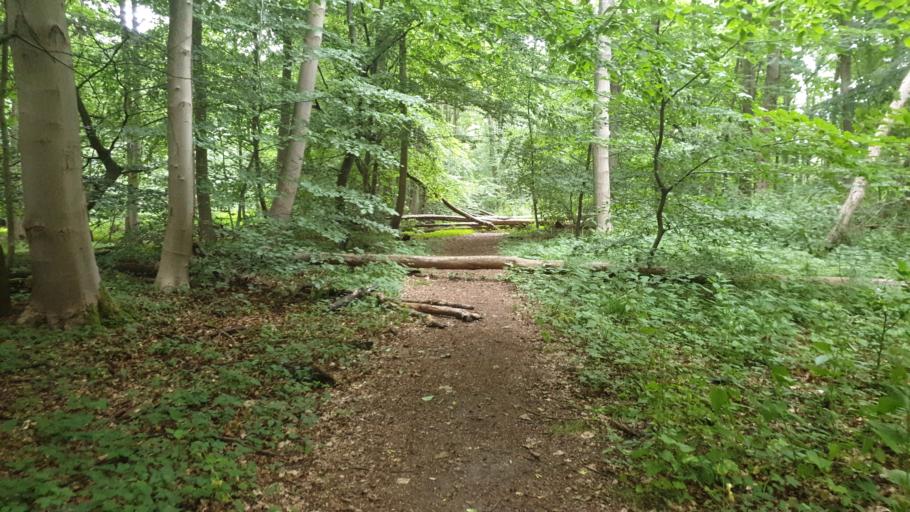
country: DE
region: Mecklenburg-Vorpommern
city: Werdervorstadt
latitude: 53.6446
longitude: 11.4528
